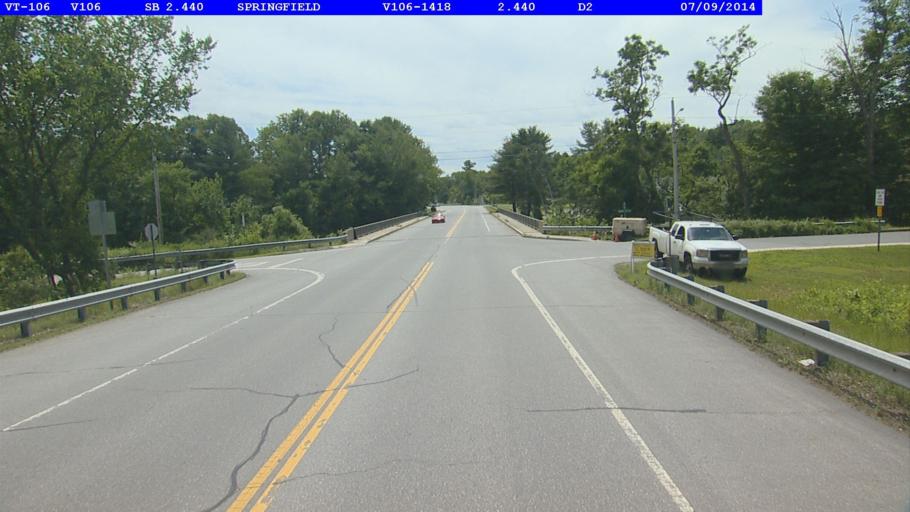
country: US
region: Vermont
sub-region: Windsor County
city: Springfield
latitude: 43.3333
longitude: -72.5171
